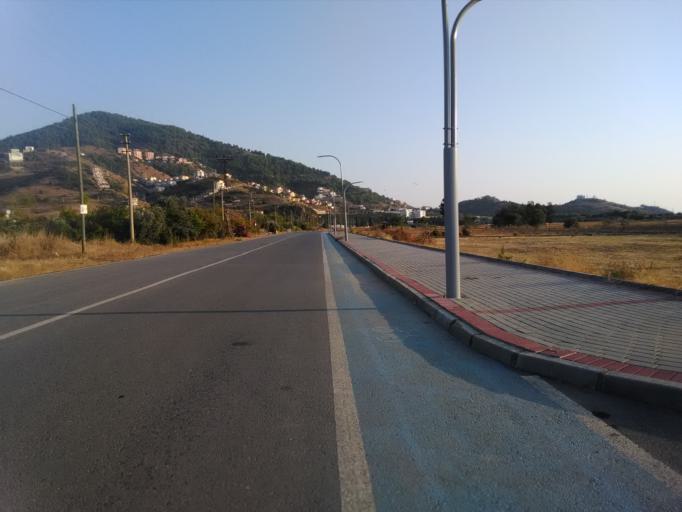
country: TR
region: Antalya
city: Gazipasa
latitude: 36.2454
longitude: 32.2962
